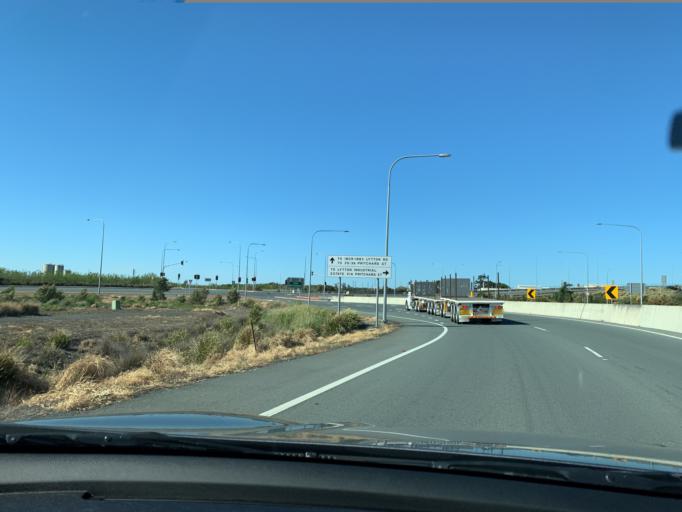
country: AU
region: Queensland
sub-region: Brisbane
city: Wynnum
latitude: -27.4268
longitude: 153.1450
